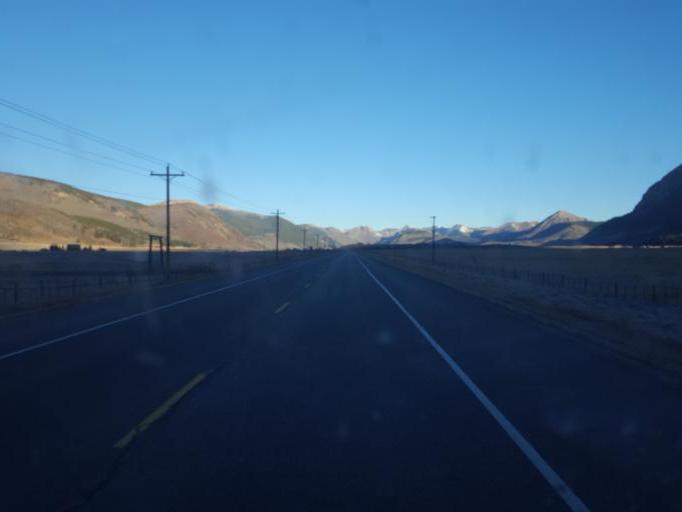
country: US
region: Colorado
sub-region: Gunnison County
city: Crested Butte
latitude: 38.8275
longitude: -106.9216
